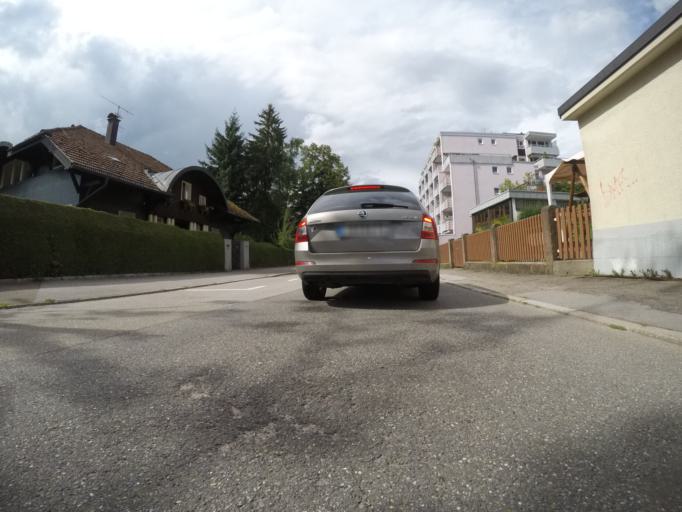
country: DE
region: Baden-Wuerttemberg
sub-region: Karlsruhe Region
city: Freudenstadt
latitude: 48.4631
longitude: 8.4087
